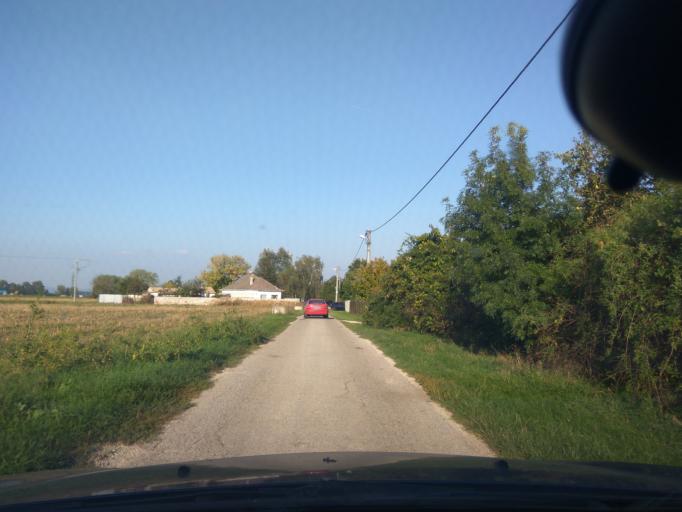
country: SK
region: Trnavsky
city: Vrbove
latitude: 48.5829
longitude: 17.7601
